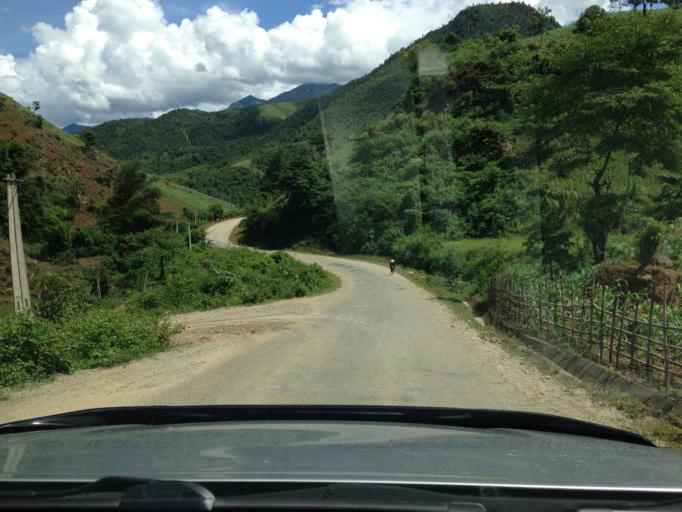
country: VN
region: Lao Cai
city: Thi Tran Khanh Yen
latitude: 22.0447
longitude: 104.0990
